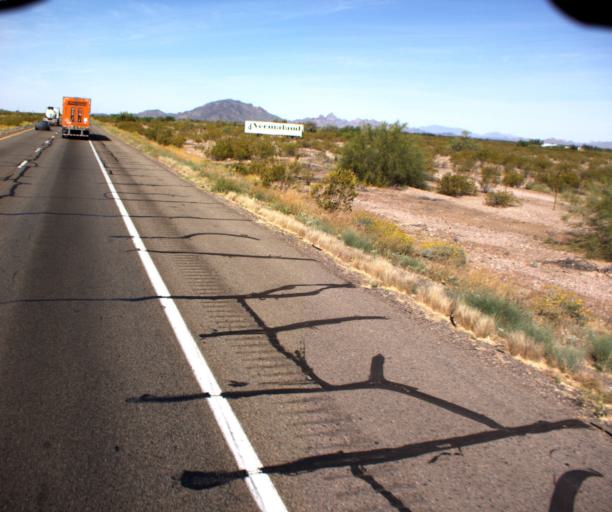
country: US
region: Arizona
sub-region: Maricopa County
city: Buckeye
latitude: 33.5022
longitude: -112.9595
